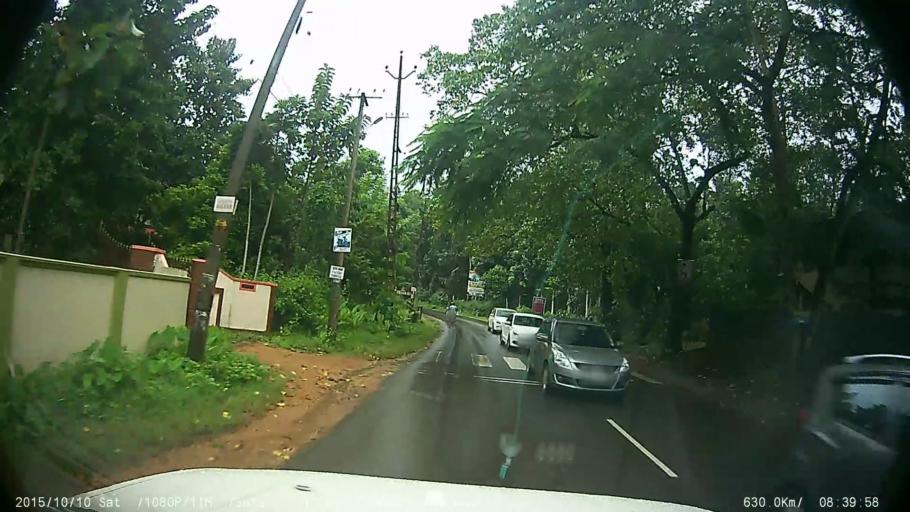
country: IN
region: Kerala
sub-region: Kottayam
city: Palackattumala
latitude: 9.7569
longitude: 76.5539
